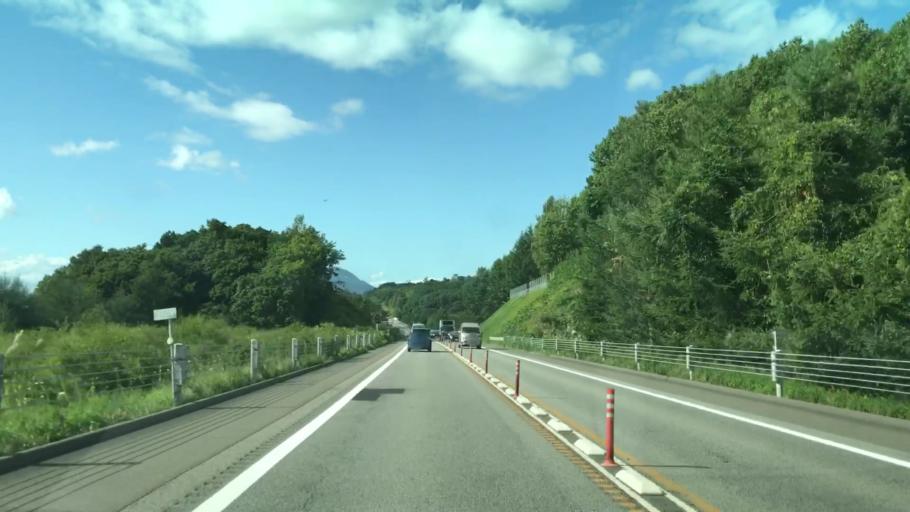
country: JP
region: Hokkaido
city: Date
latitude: 42.4299
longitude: 140.9255
